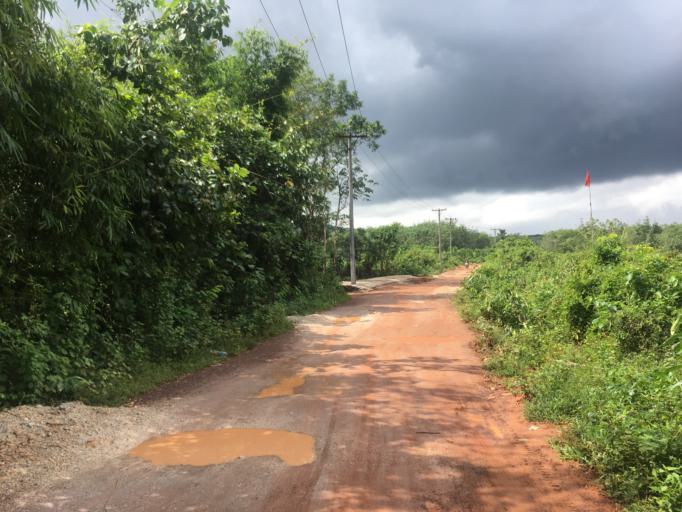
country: MM
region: Mon
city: Mawlamyine
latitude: 16.4600
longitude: 97.6894
